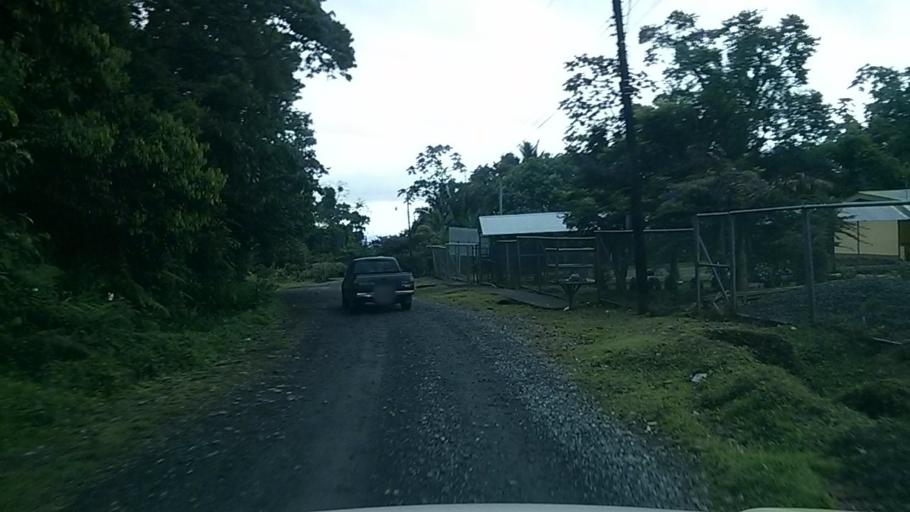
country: CR
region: Limon
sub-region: Canton de Pococi
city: Guapiles
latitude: 10.1701
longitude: -83.7836
